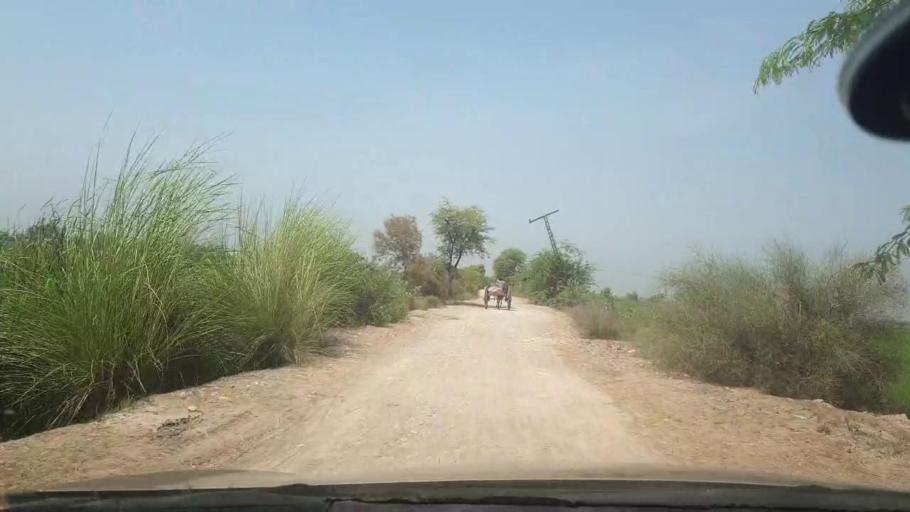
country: PK
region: Sindh
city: Shahdadkot
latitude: 27.7568
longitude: 67.9413
